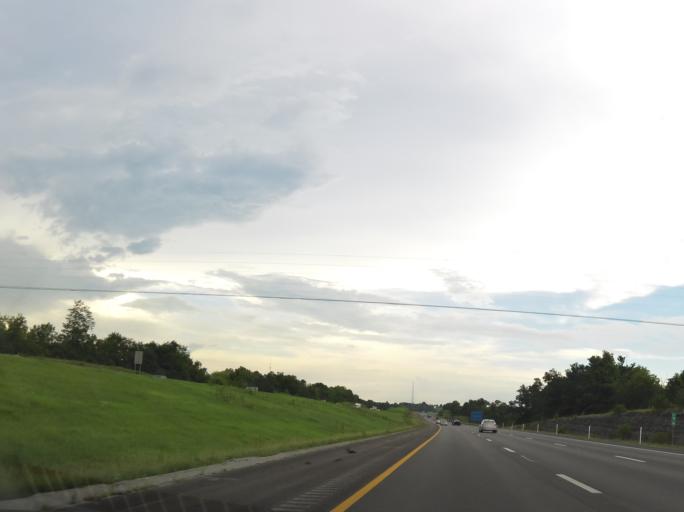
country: US
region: Kentucky
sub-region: Madison County
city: Richmond
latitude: 37.8609
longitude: -84.3319
